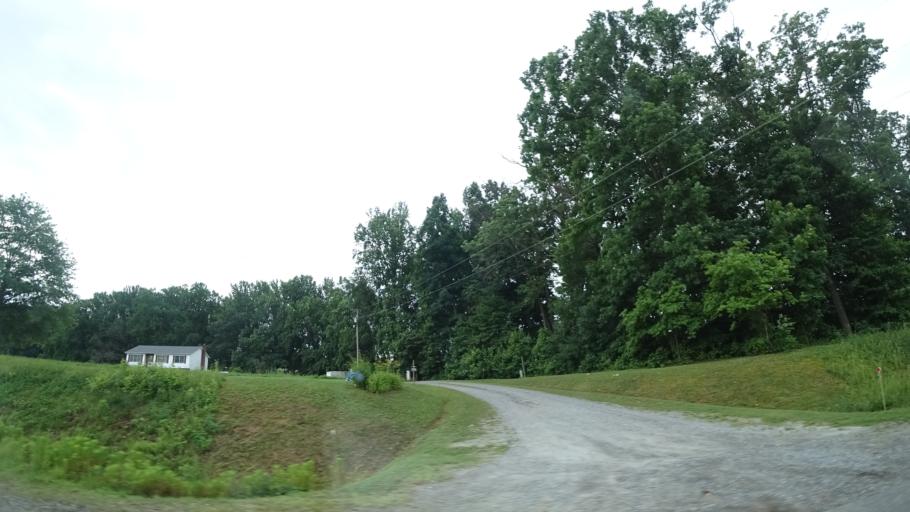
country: US
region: Virginia
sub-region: Spotsylvania County
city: Spotsylvania Courthouse
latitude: 38.1601
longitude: -77.6692
